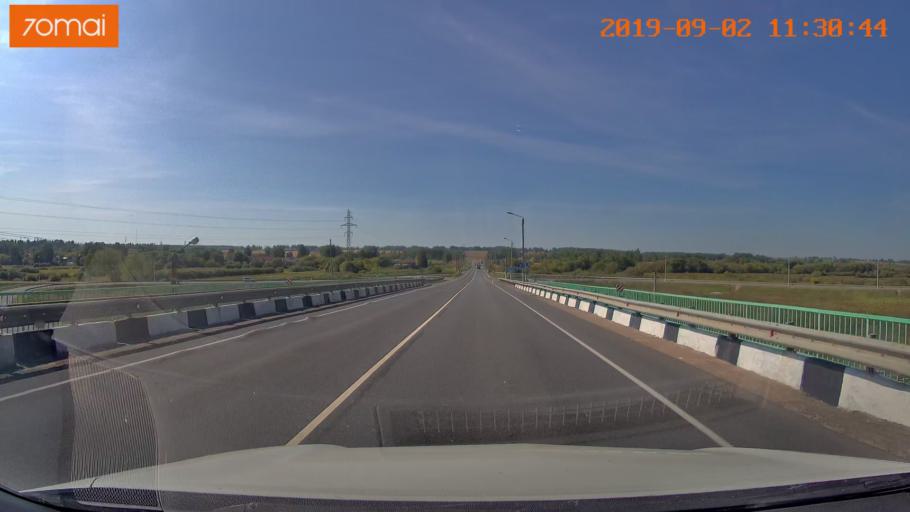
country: RU
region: Smolensk
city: Oster
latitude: 53.9812
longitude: 32.8277
